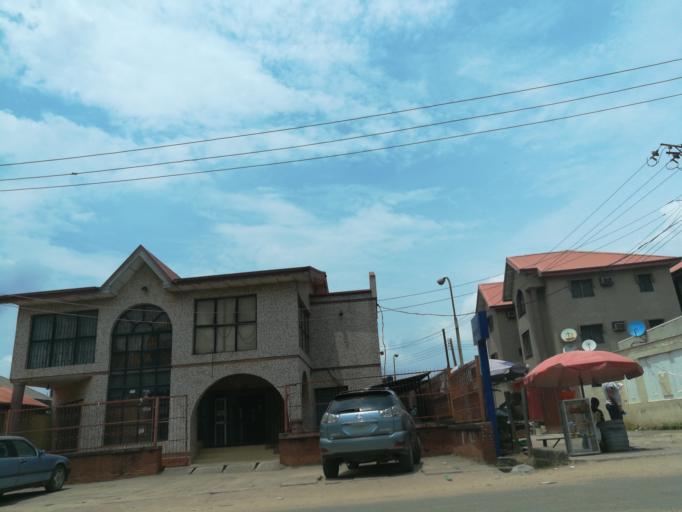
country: NG
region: Lagos
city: Oshodi
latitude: 6.5480
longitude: 3.3285
